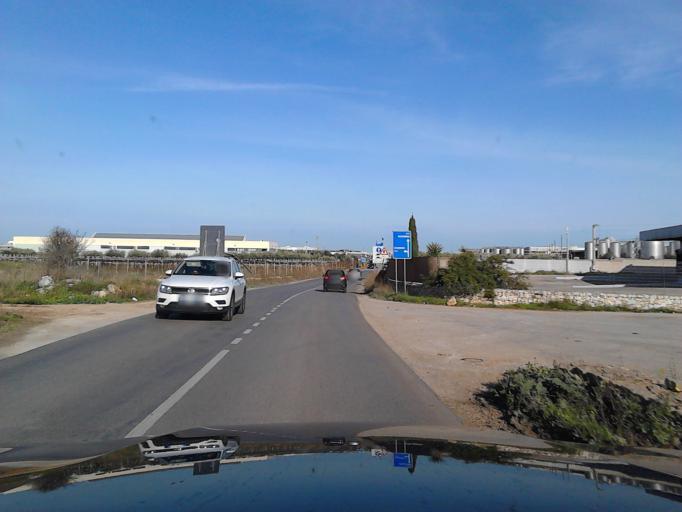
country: IT
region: Apulia
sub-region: Provincia di Bari
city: Noicattaro
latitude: 41.0200
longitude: 16.9684
